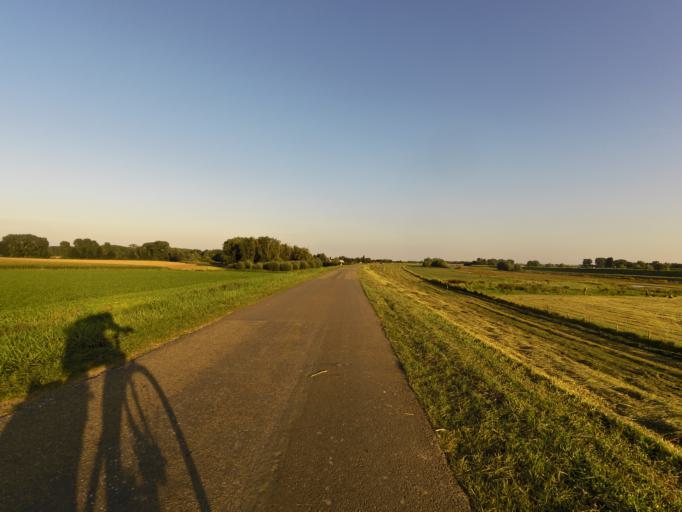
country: NL
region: Gelderland
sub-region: Gemeente Duiven
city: Duiven
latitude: 51.9037
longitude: 6.0189
